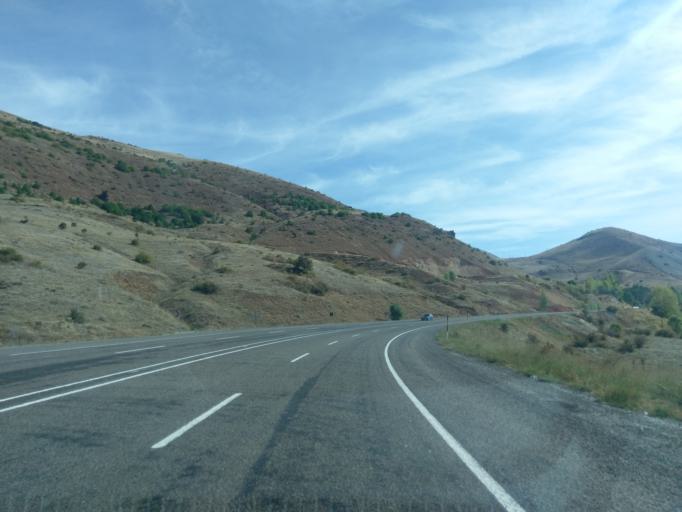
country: TR
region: Sivas
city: Akincilar
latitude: 39.8618
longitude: 38.3440
